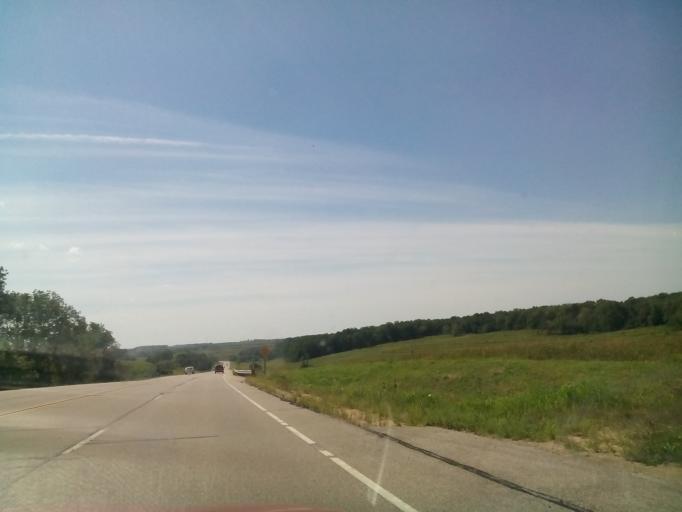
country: US
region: Wisconsin
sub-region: Green County
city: New Glarus
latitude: 42.7852
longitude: -89.6279
